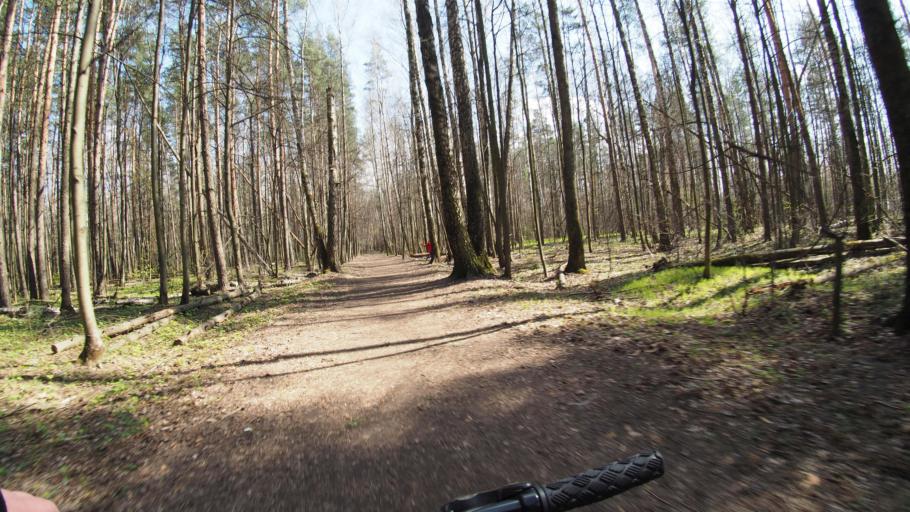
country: RU
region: Moskovskaya
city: Ramenskoye
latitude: 55.5807
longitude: 38.2287
